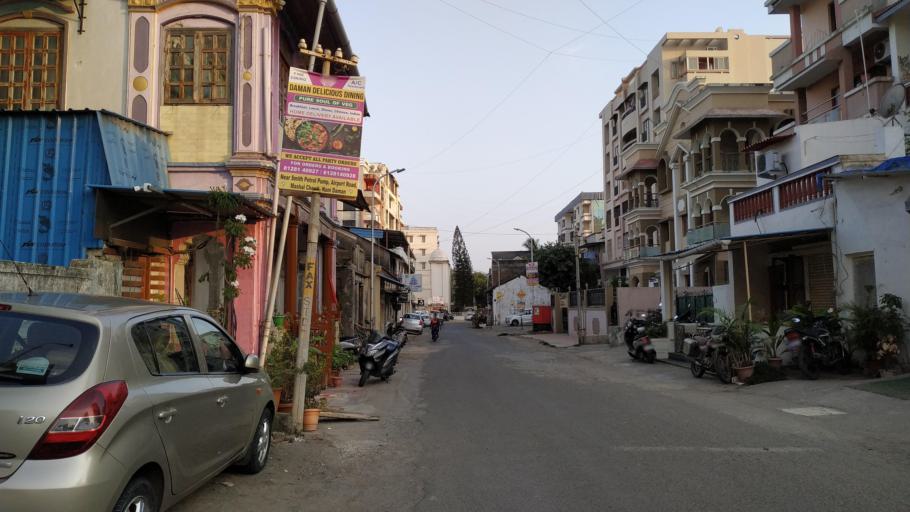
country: IN
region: Daman and Diu
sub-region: Daman District
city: Daman
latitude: 20.4158
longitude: 72.8336
